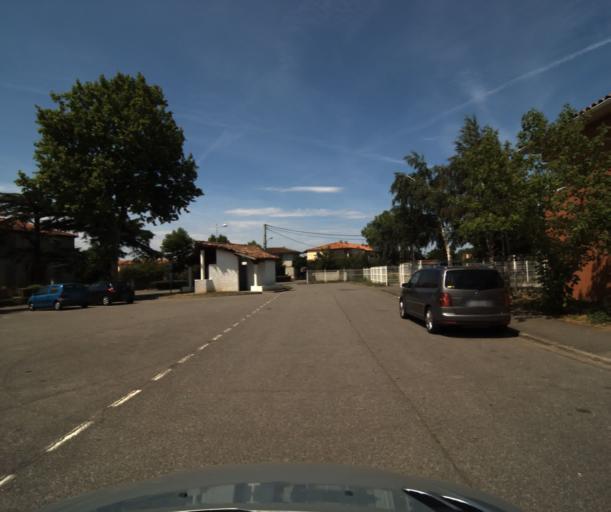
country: FR
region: Midi-Pyrenees
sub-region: Departement de la Haute-Garonne
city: Labastidette
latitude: 43.4602
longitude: 1.2456
